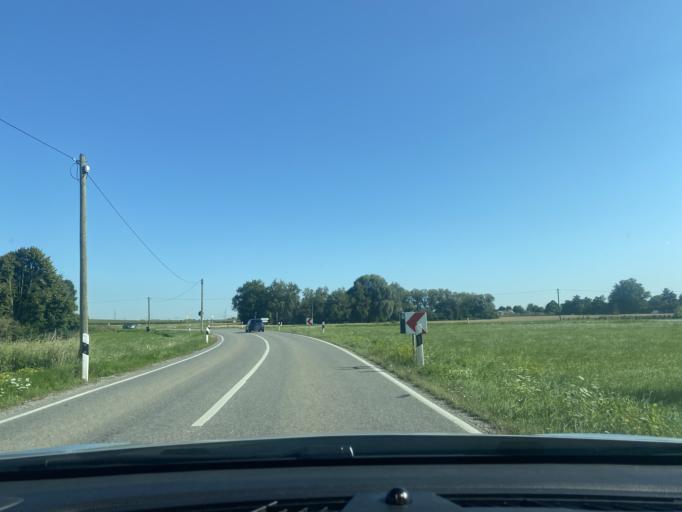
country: DE
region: Bavaria
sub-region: Upper Bavaria
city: Erding
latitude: 48.3228
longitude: 11.8941
